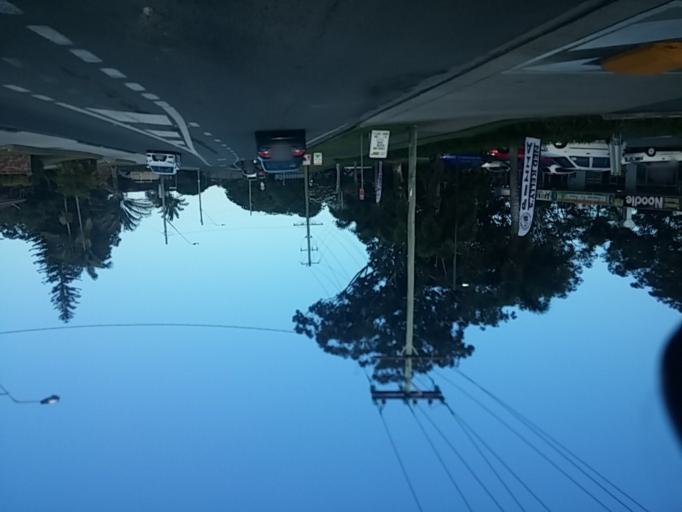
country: AU
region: New South Wales
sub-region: Tweed
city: Tweed Heads West
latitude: -28.1869
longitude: 153.5284
